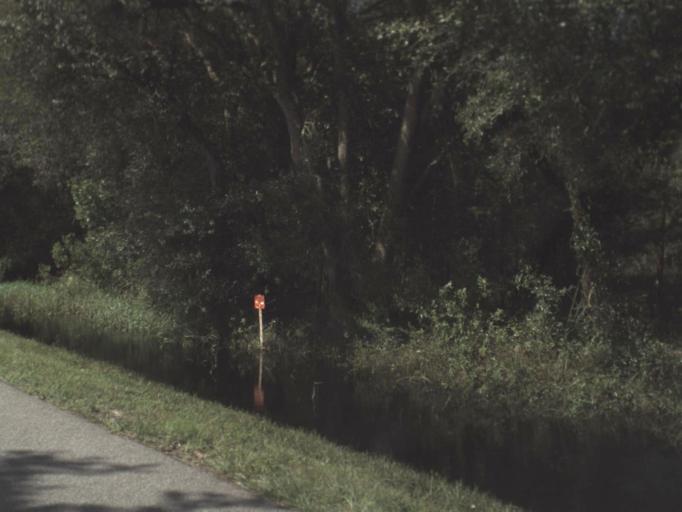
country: US
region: Florida
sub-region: Sarasota County
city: Lake Sarasota
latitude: 27.3808
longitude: -82.2367
